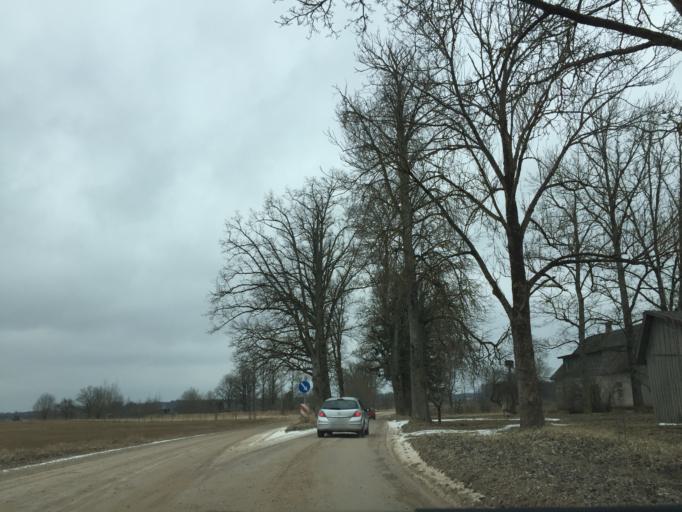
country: LV
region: Kegums
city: Kegums
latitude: 56.7692
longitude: 24.7723
